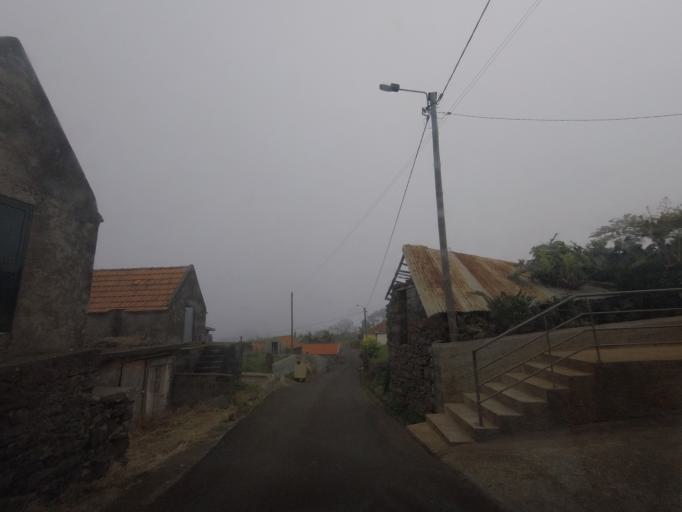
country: PT
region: Madeira
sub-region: Calheta
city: Faja da Ovelha
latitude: 32.7638
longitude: -17.2192
